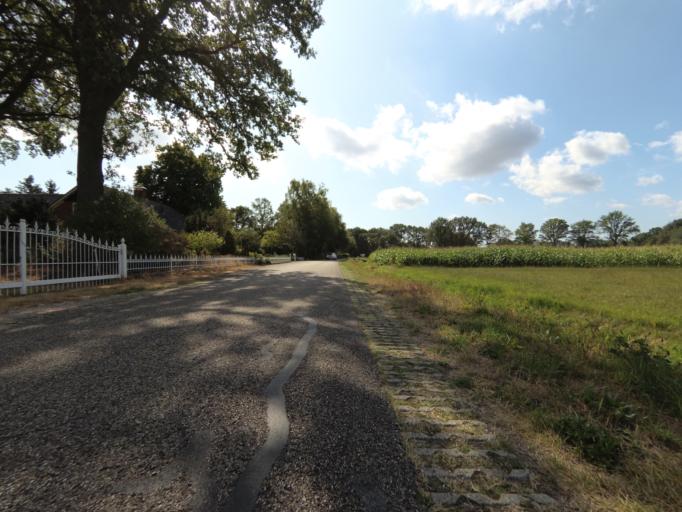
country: NL
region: Overijssel
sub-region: Gemeente Oldenzaal
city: Oldenzaal
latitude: 52.2995
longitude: 6.8804
